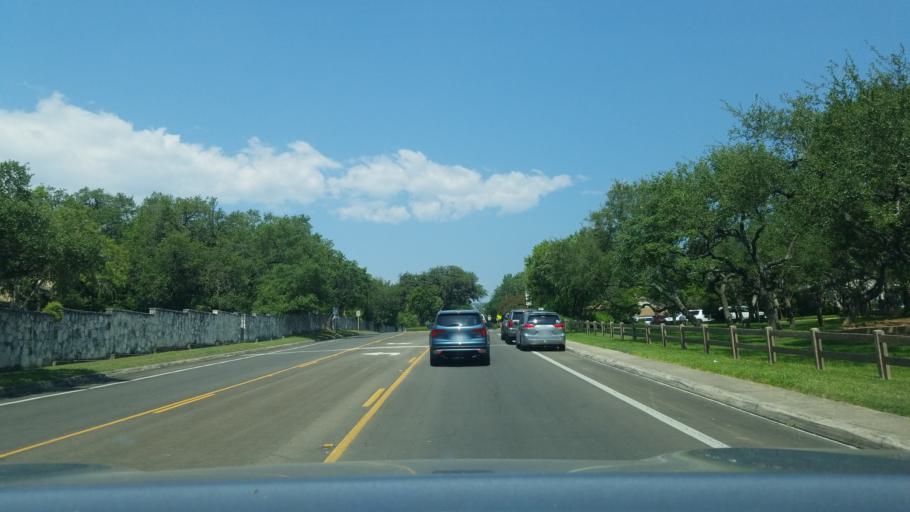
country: US
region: Texas
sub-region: Bexar County
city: Hollywood Park
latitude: 29.6297
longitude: -98.4503
